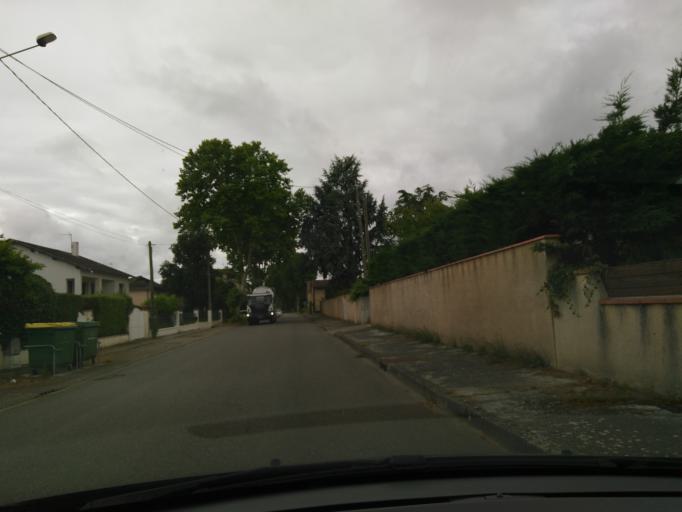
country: FR
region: Midi-Pyrenees
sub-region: Departement de la Haute-Garonne
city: Grenade
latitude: 43.7763
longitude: 1.2895
